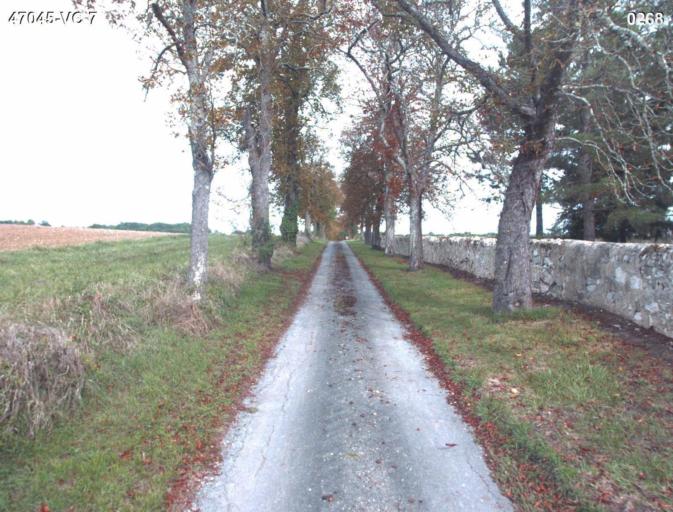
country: FR
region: Aquitaine
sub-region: Departement du Lot-et-Garonne
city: Nerac
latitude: 44.1378
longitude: 0.4320
